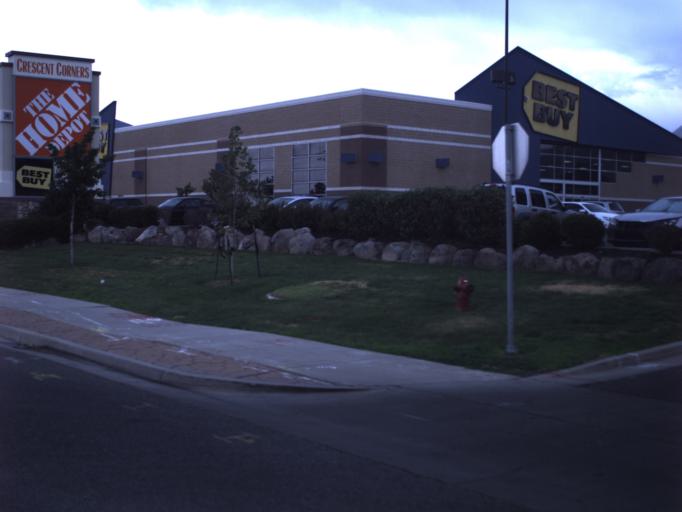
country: US
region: Utah
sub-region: Salt Lake County
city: White City
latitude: 40.5451
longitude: -111.8910
